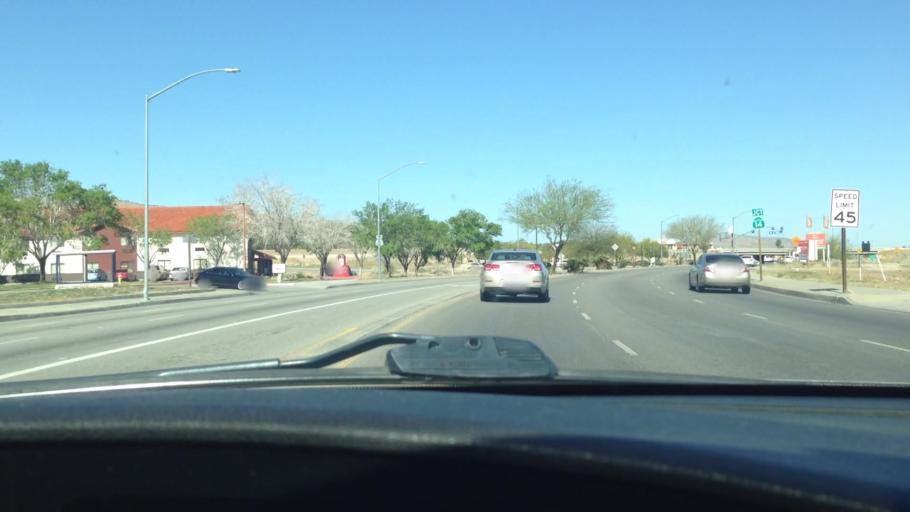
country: US
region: California
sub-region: Los Angeles County
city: Palmdale
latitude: 34.5799
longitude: -118.1299
